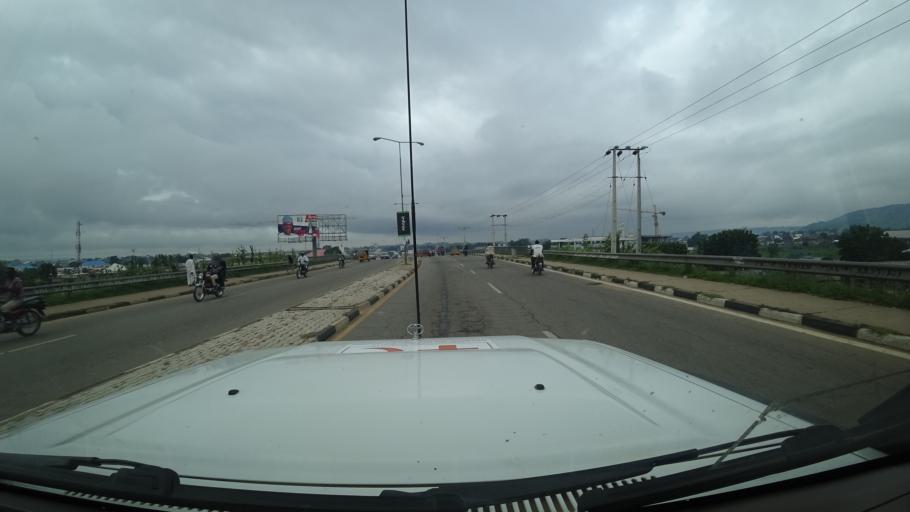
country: NG
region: Niger
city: Minna
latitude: 9.6128
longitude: 6.5493
